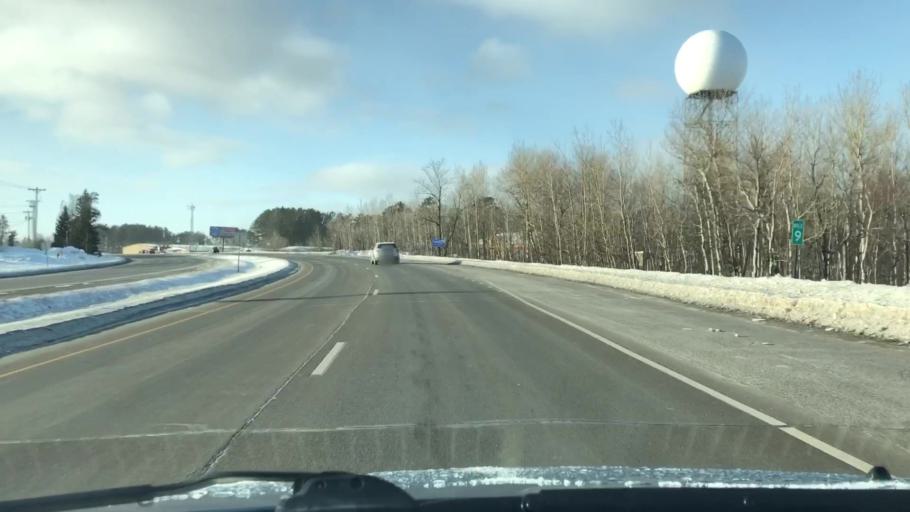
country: US
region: Minnesota
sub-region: Saint Louis County
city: Hermantown
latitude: 46.8357
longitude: -92.2088
